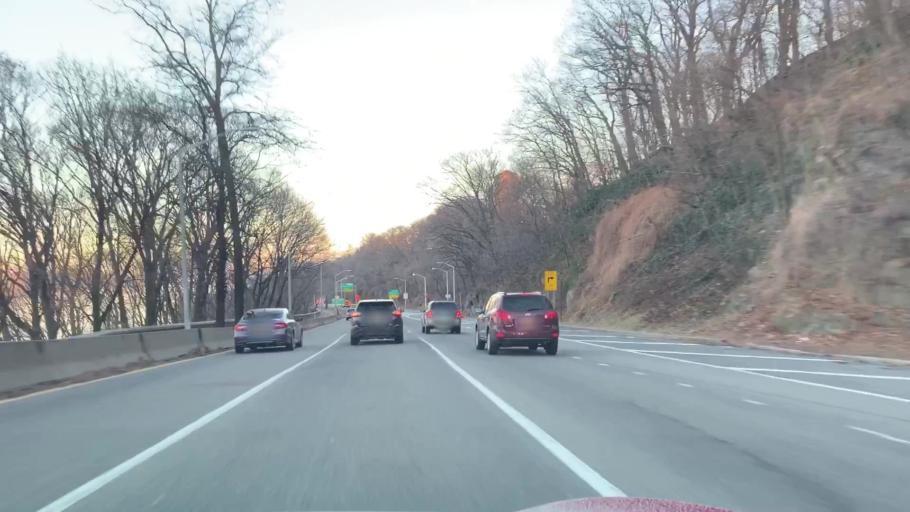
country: US
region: New York
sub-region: New York County
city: Inwood
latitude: 40.8618
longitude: -73.9346
